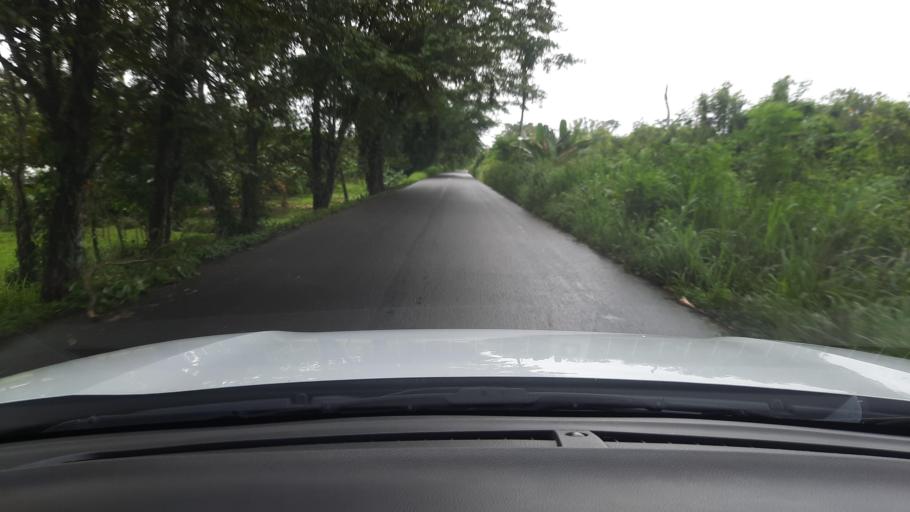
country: CR
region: Alajuela
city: San Jose
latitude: 10.9280
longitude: -85.0800
